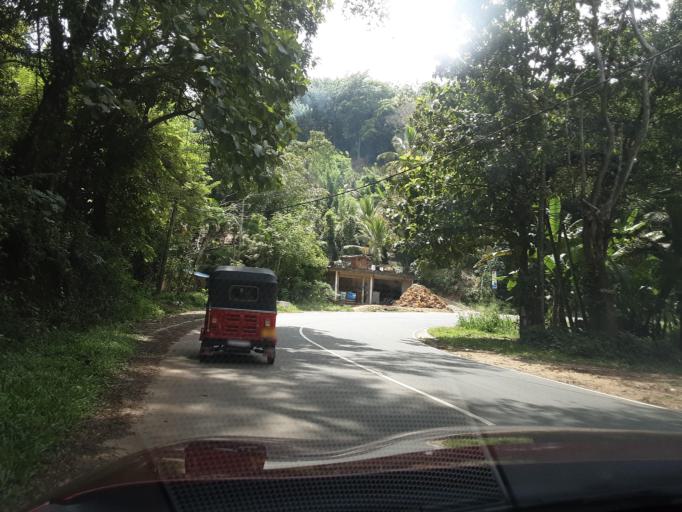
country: LK
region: Uva
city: Monaragala
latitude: 6.8968
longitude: 81.2517
